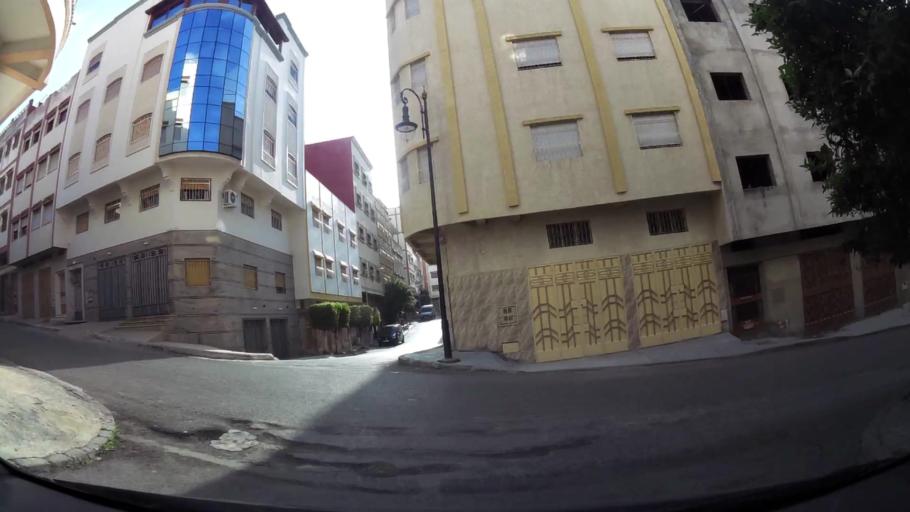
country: MA
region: Tanger-Tetouan
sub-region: Tanger-Assilah
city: Tangier
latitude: 35.7626
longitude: -5.8350
